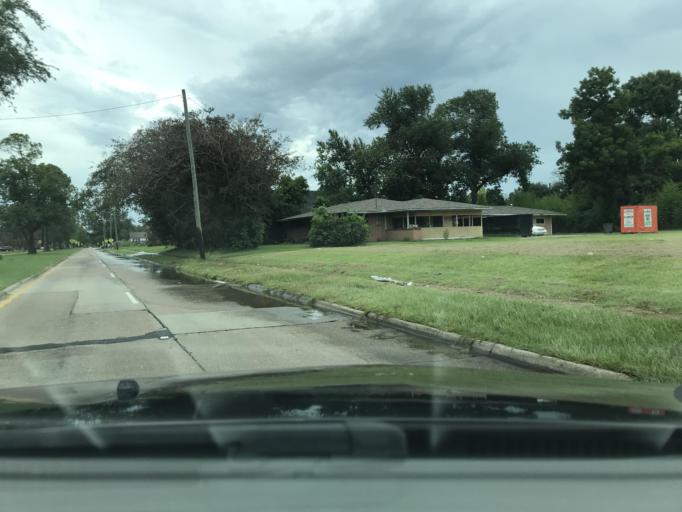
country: US
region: Louisiana
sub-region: Calcasieu Parish
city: Lake Charles
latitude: 30.2035
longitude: -93.2042
